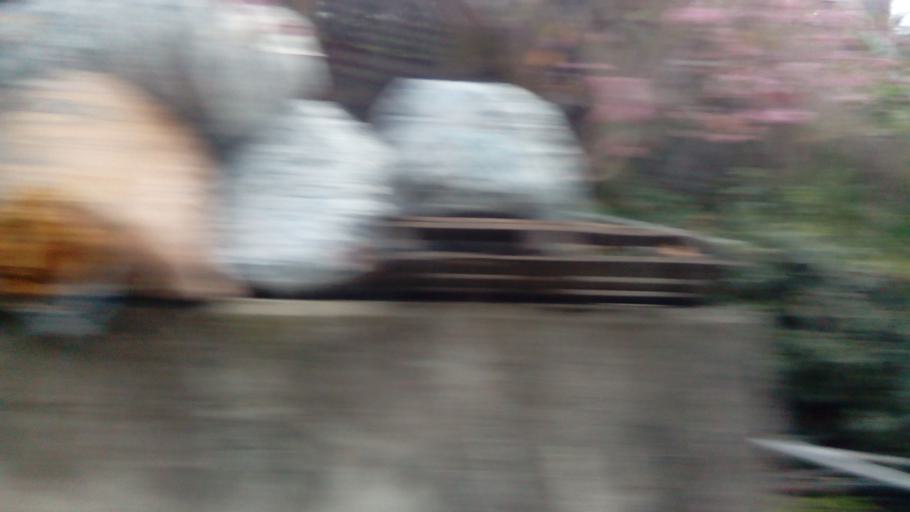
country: TW
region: Taiwan
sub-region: Nantou
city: Puli
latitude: 24.2596
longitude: 121.2565
